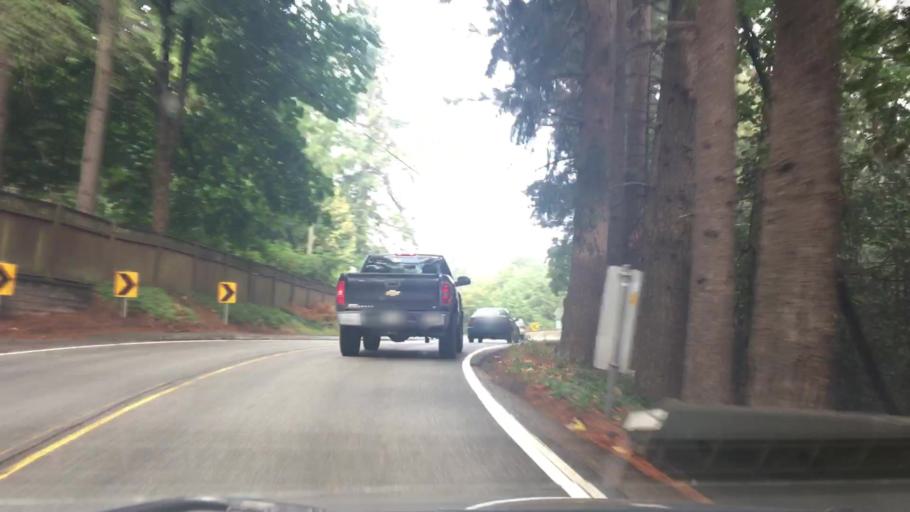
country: CA
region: British Columbia
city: Langley
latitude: 49.1037
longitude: -122.5531
